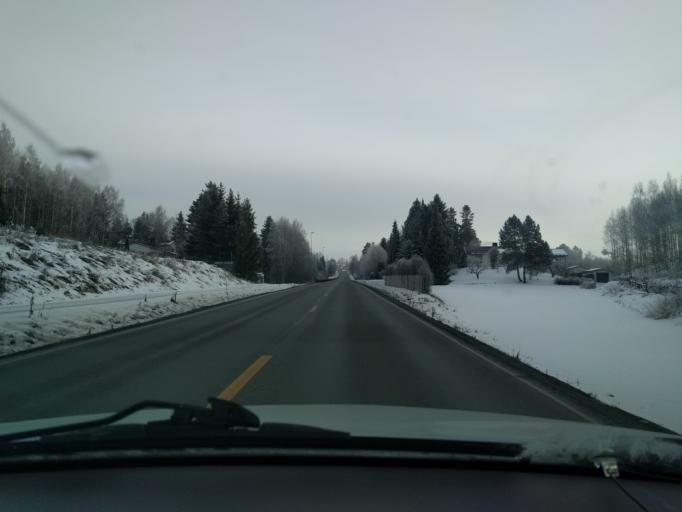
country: NO
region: Hedmark
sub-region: Hamar
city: Hamar
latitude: 60.8085
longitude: 11.1615
